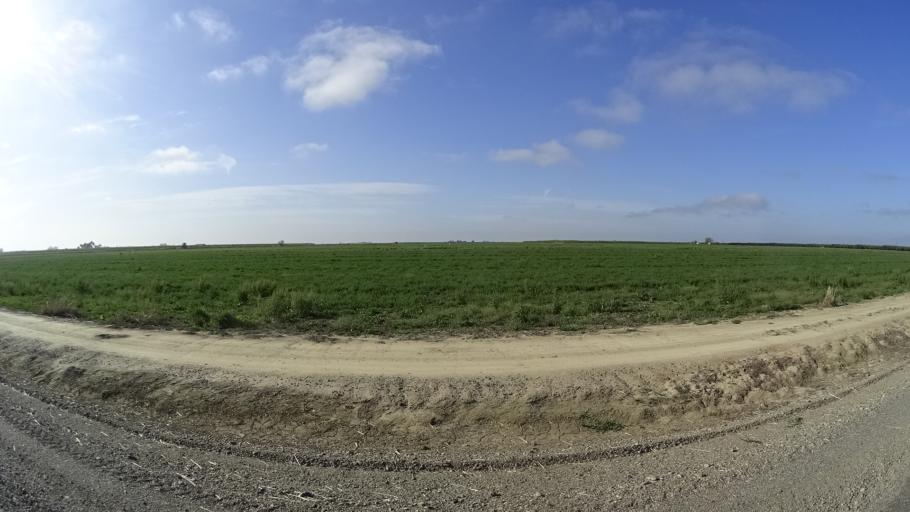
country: US
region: California
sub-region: Glenn County
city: Willows
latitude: 39.5822
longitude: -122.1309
